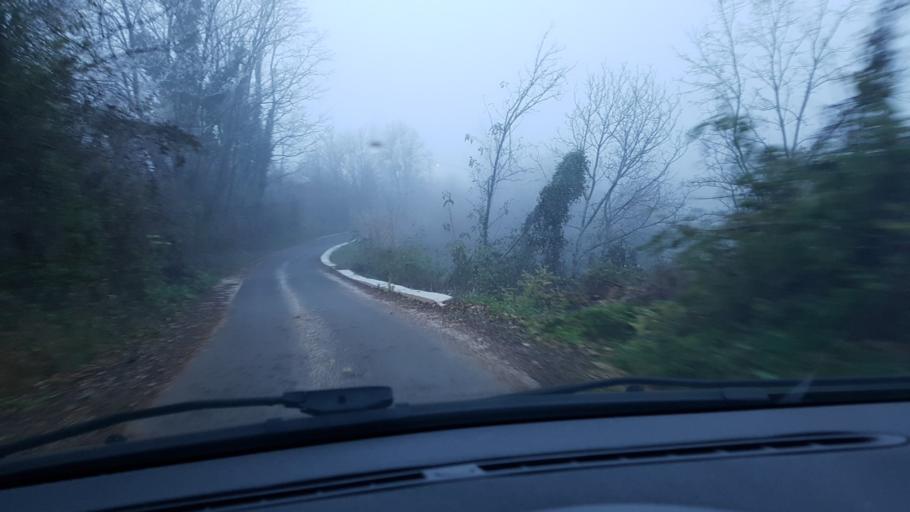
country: HR
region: Krapinsko-Zagorska
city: Pregrada
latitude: 46.1931
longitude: 15.7461
